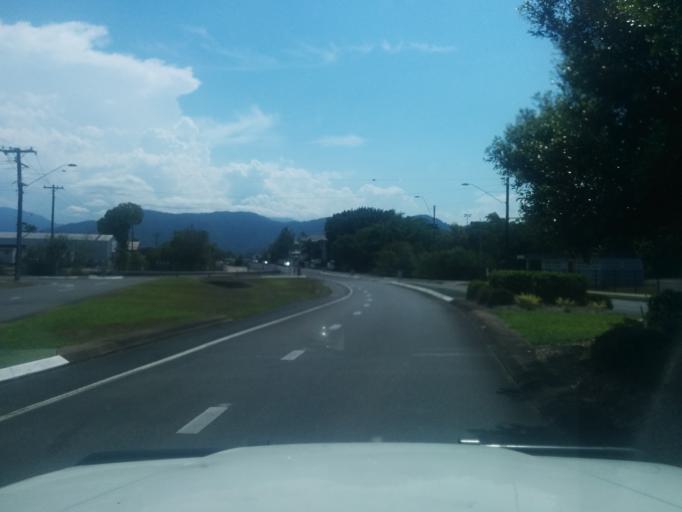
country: AU
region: Queensland
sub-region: Cairns
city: Cairns
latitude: -16.9314
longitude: 145.7677
